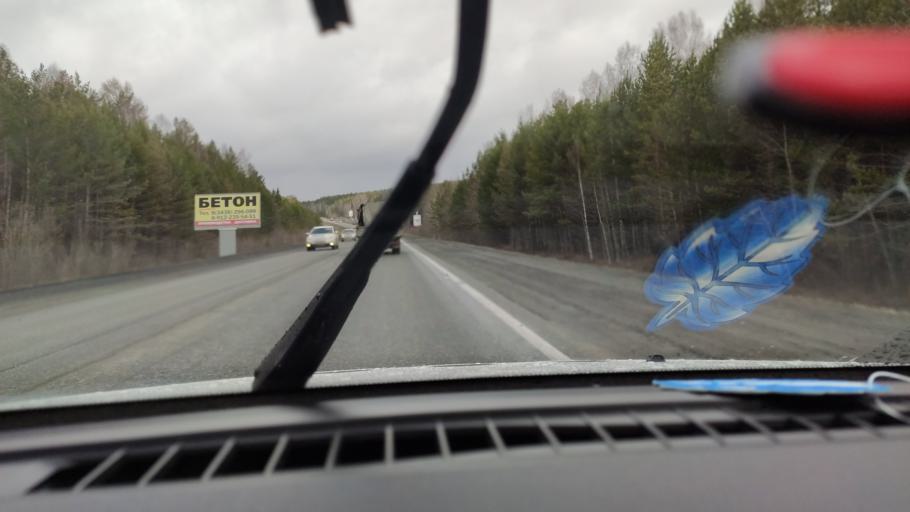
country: RU
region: Sverdlovsk
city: Talitsa
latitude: 56.8659
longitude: 60.0470
